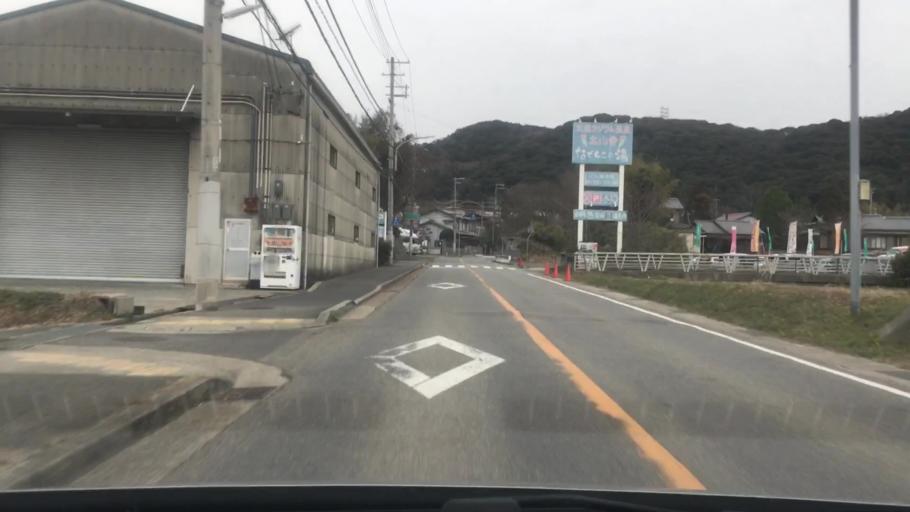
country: JP
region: Hyogo
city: Akashi
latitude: 34.6959
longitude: 135.0632
